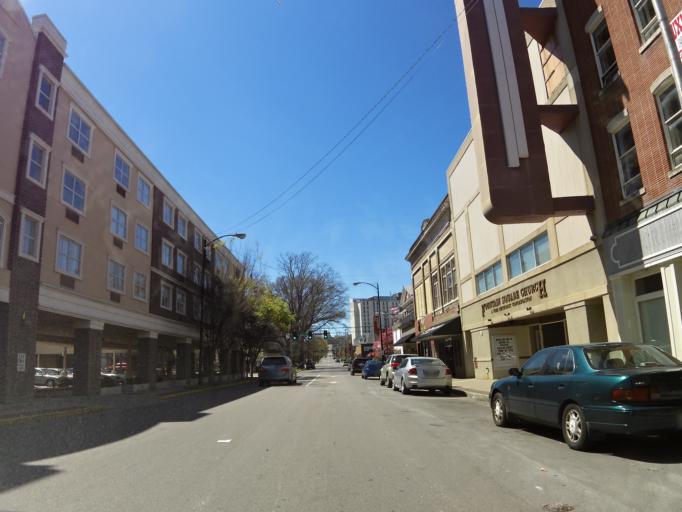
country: US
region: Kentucky
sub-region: Warren County
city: Bowling Green
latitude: 36.9934
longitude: -86.4422
